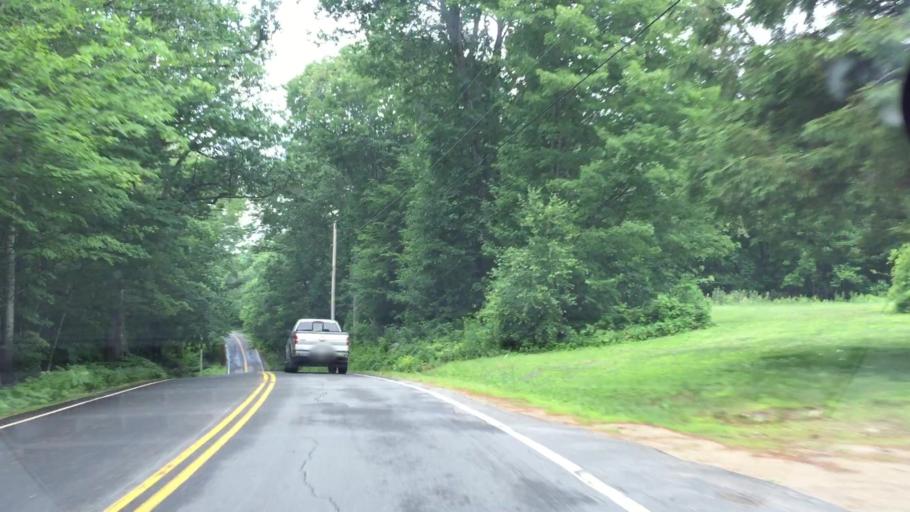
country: US
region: New Hampshire
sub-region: Carroll County
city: Sandwich
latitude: 43.8038
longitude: -71.4762
